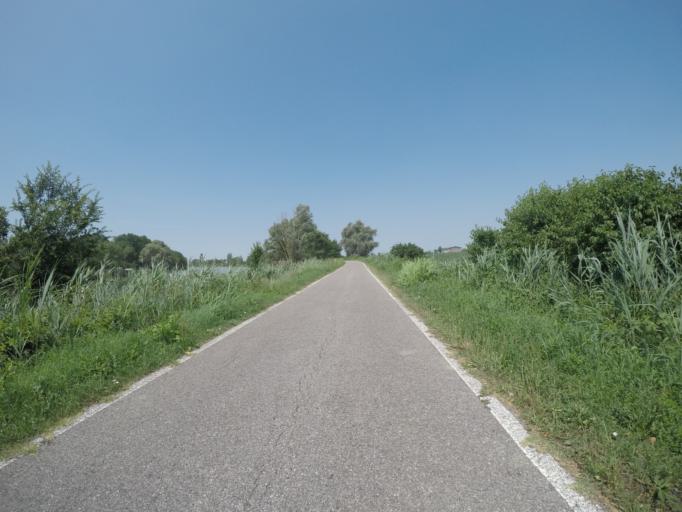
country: IT
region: Veneto
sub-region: Provincia di Rovigo
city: Villamarzana
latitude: 45.0099
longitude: 11.6646
